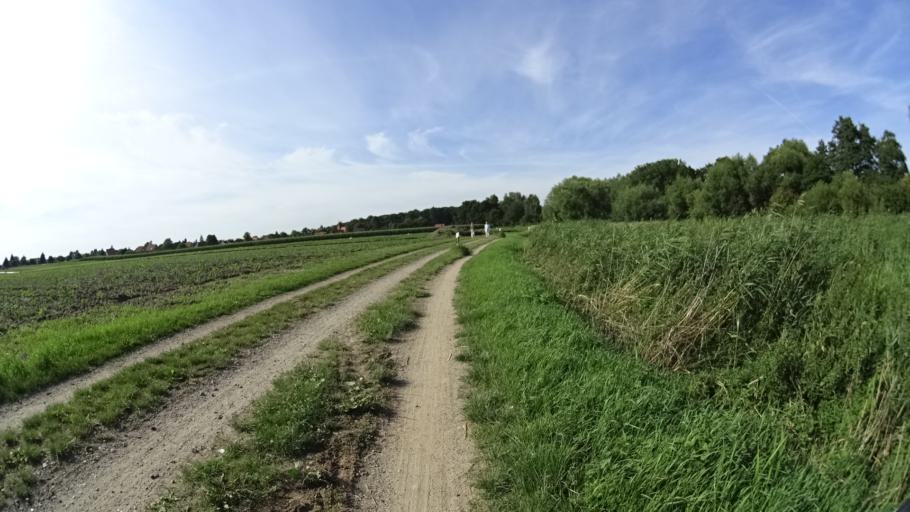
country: DE
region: Lower Saxony
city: Bardowick
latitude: 53.2870
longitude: 10.4018
